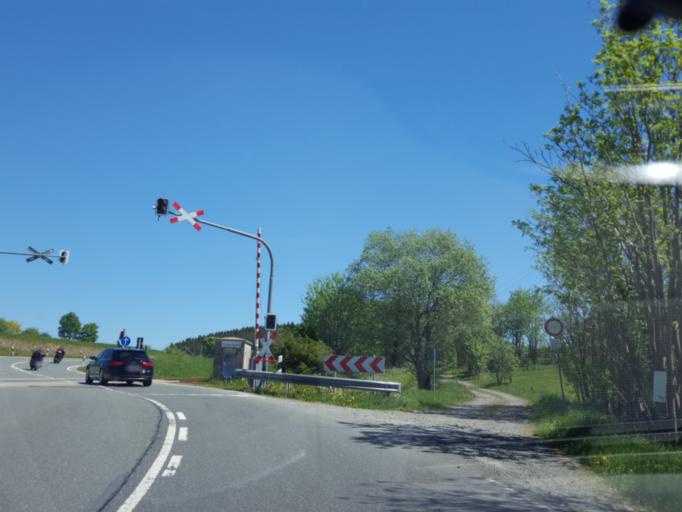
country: DE
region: North Rhine-Westphalia
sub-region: Regierungsbezirk Arnsberg
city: Winterberg
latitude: 51.2053
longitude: 8.5268
